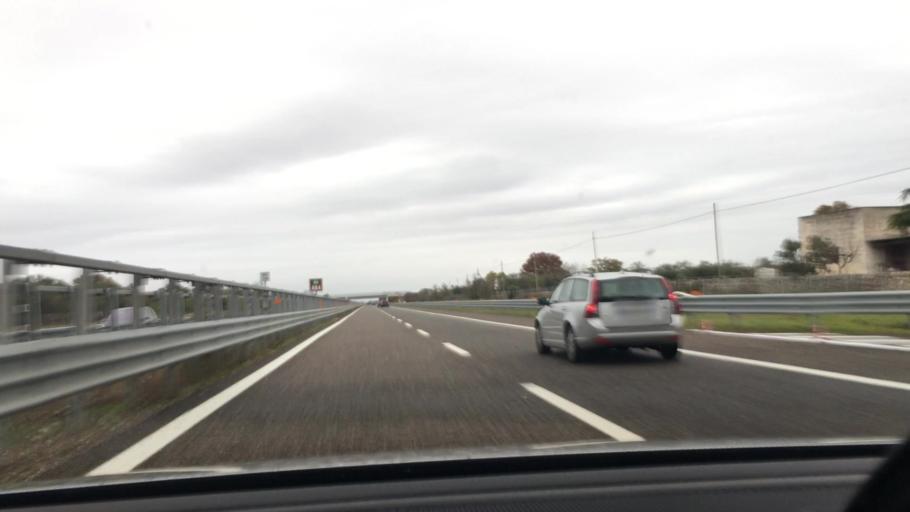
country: IT
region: Apulia
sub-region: Provincia di Bari
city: Gioia del Colle
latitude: 40.7441
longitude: 16.9140
